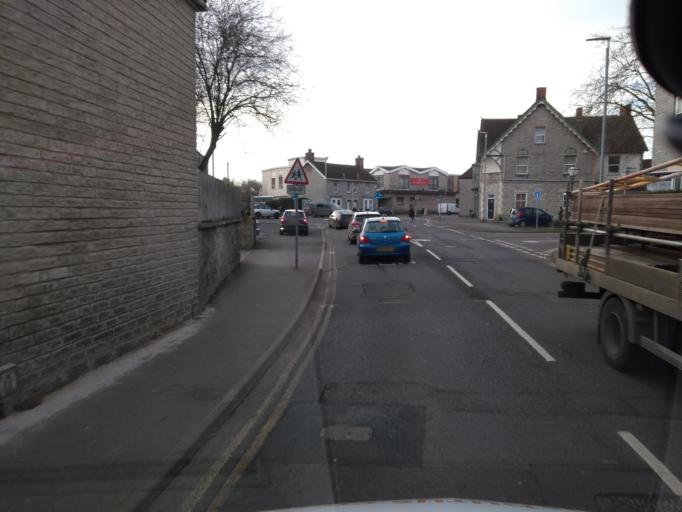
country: GB
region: England
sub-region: Somerset
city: Street
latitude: 51.1307
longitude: -2.7359
